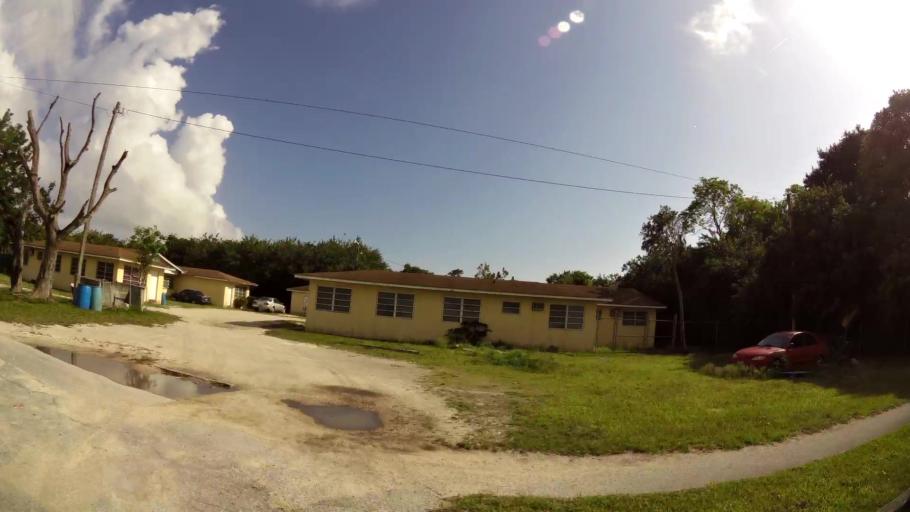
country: BS
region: Freeport
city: Lucaya
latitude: 26.5217
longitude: -78.6773
